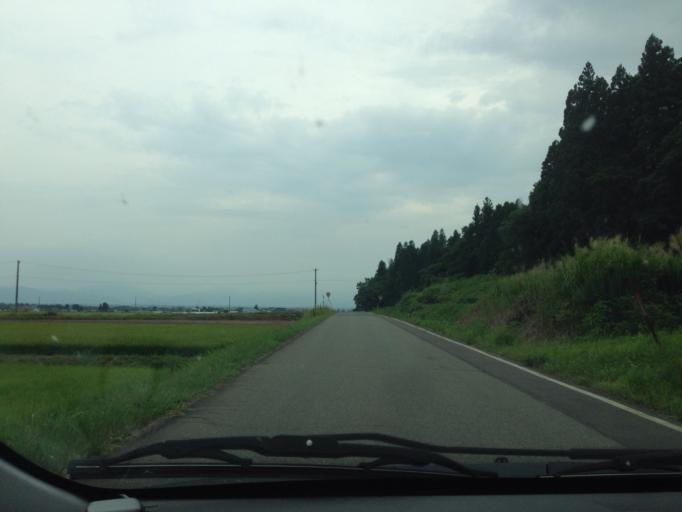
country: JP
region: Fukushima
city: Kitakata
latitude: 37.6566
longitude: 139.8461
